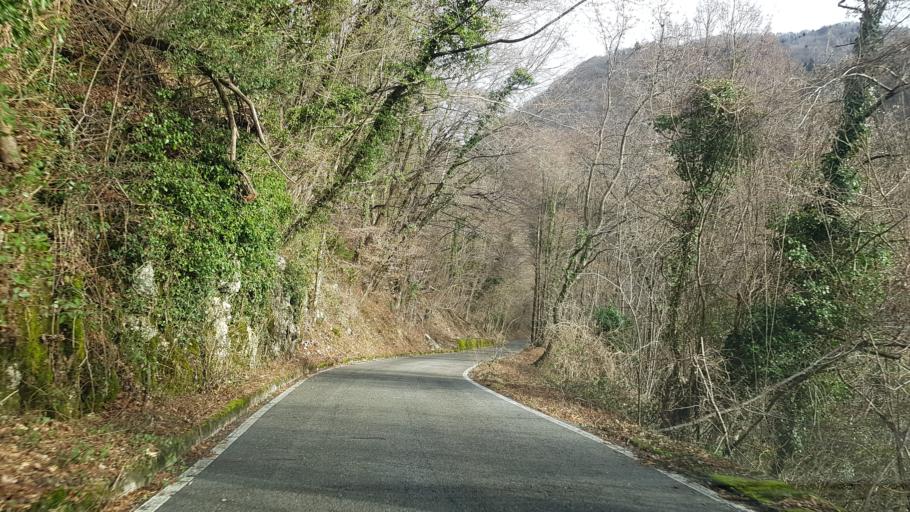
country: IT
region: Friuli Venezia Giulia
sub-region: Provincia di Udine
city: Clodig
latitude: 46.1782
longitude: 13.5753
